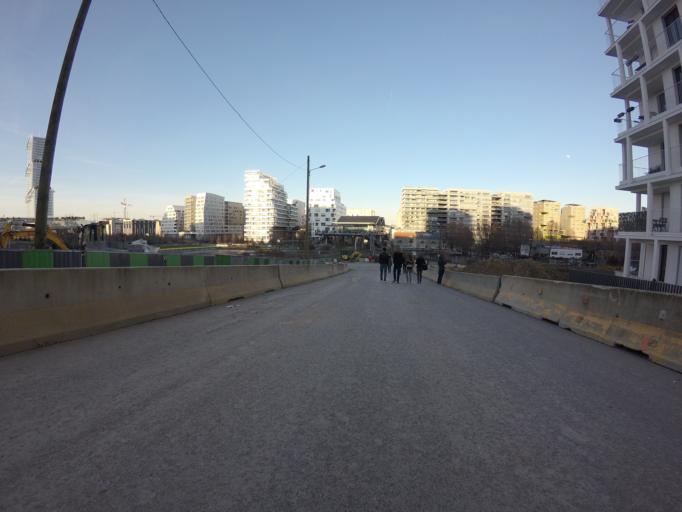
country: FR
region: Ile-de-France
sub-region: Departement des Hauts-de-Seine
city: Clichy
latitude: 48.8906
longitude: 2.3125
